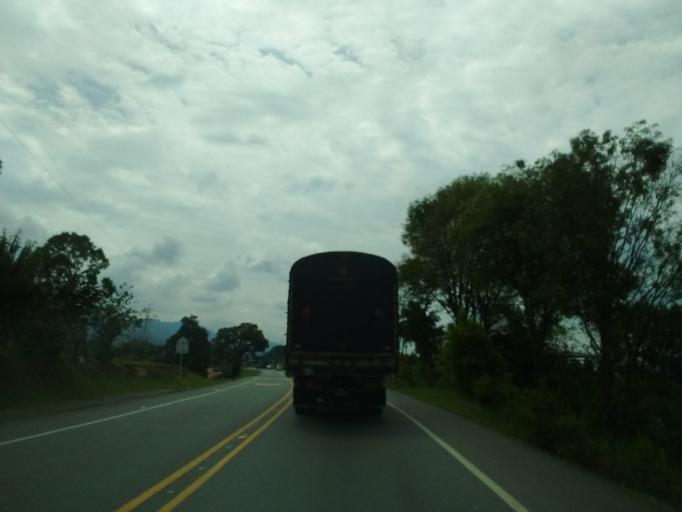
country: CO
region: Cauca
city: Morales
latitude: 2.7414
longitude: -76.5484
